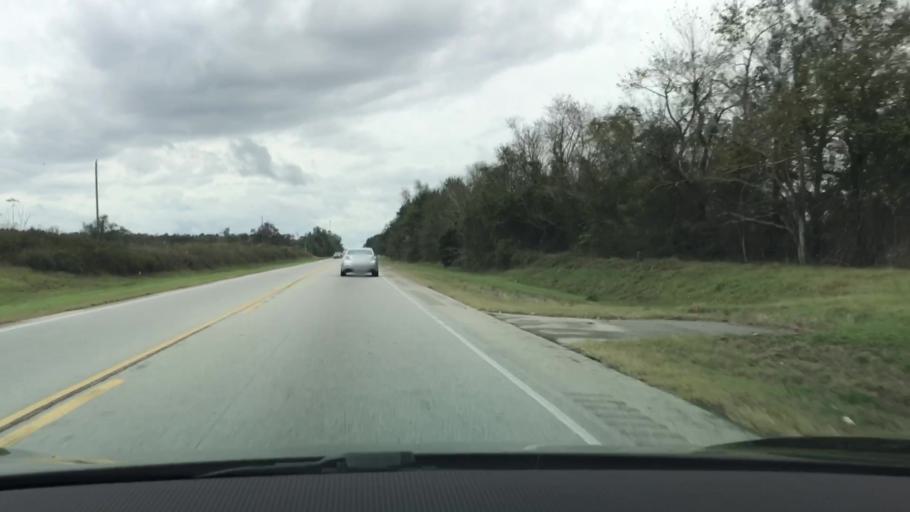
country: US
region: Georgia
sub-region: Jefferson County
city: Wadley
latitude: 32.9331
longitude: -82.3965
